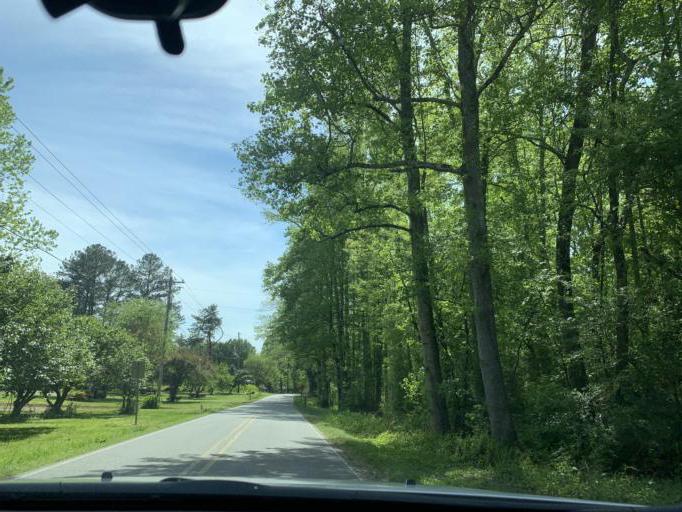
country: US
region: Georgia
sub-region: Forsyth County
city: Cumming
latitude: 34.2524
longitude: -84.2028
